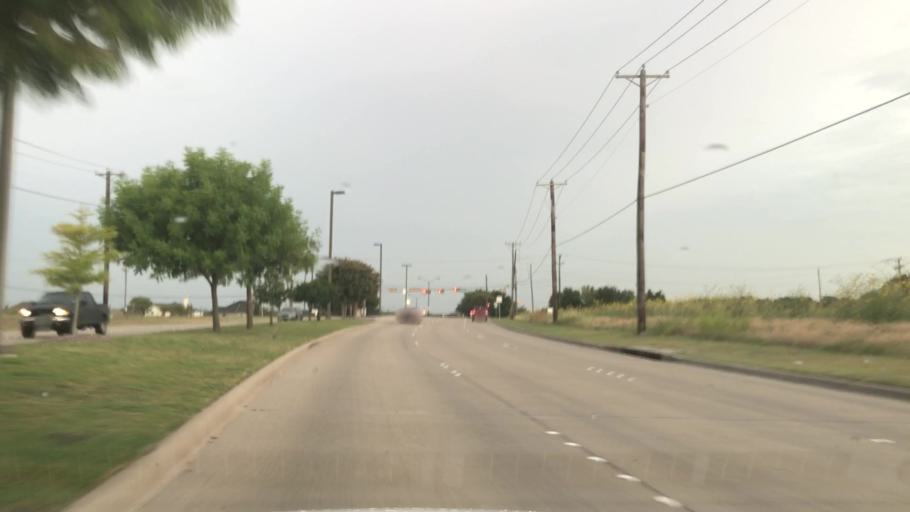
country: US
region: Texas
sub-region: Dallas County
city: Mesquite
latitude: 32.7217
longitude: -96.5441
